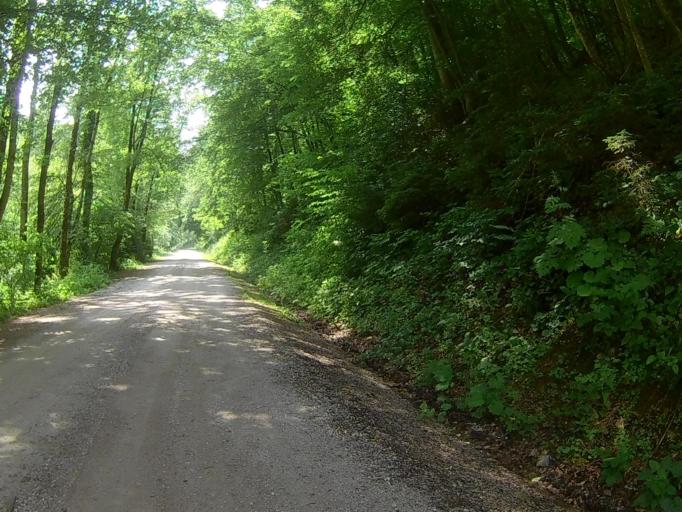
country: SI
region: Ruse
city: Bistrica ob Dravi
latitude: 46.5321
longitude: 15.5447
